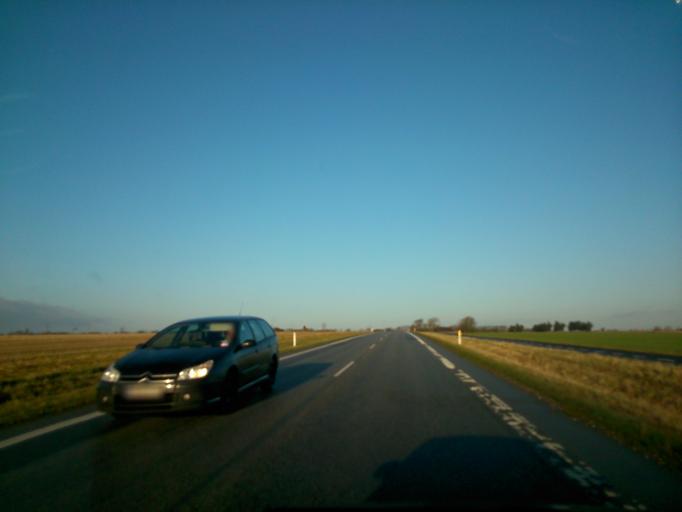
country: DK
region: Central Jutland
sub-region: Ringkobing-Skjern Kommune
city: Videbaek
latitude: 55.9914
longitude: 8.5956
